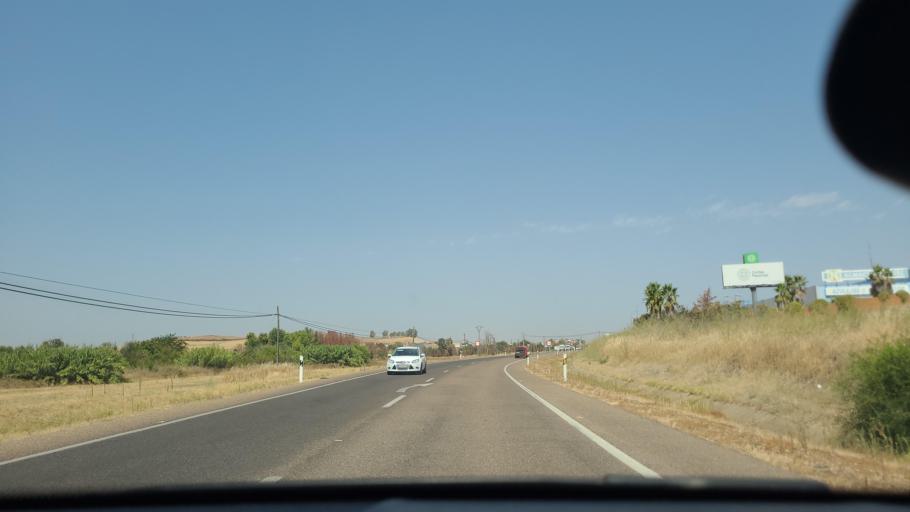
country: ES
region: Extremadura
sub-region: Provincia de Badajoz
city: Badajoz
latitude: 38.8525
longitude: -6.9425
